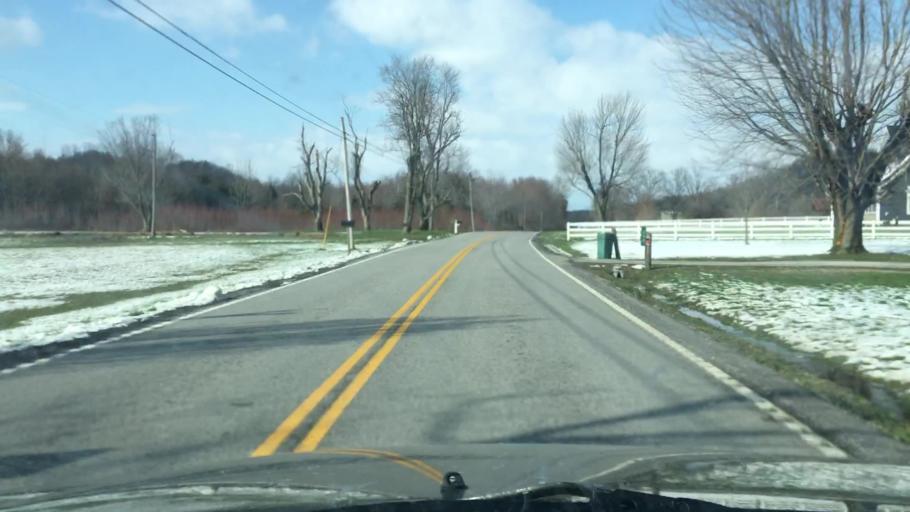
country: US
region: Kentucky
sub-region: Marion County
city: Lebanon
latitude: 37.5173
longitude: -85.3025
